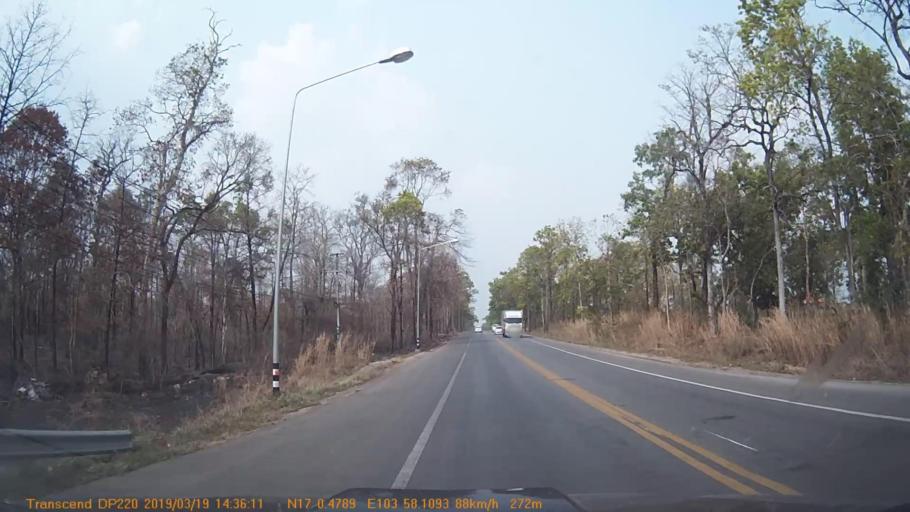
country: TH
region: Sakon Nakhon
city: Phu Phan
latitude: 17.0081
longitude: 103.9686
